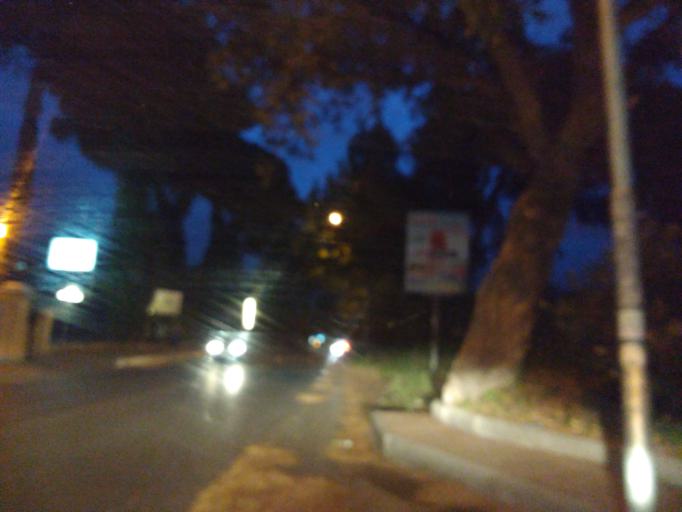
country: IT
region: Latium
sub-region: Citta metropolitana di Roma Capitale
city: Anzio
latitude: 41.4646
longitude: 12.6222
